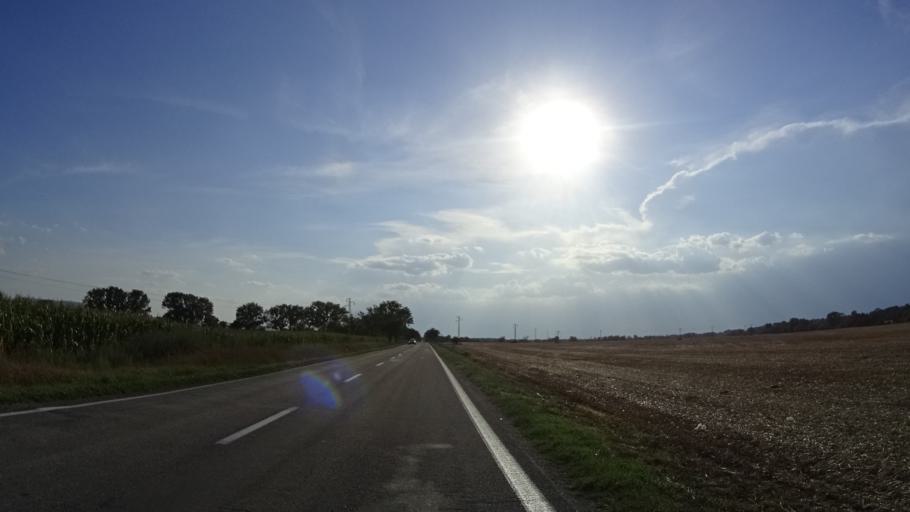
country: HU
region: Komarom-Esztergom
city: Nyergesujfalu
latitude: 47.7872
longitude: 18.5965
